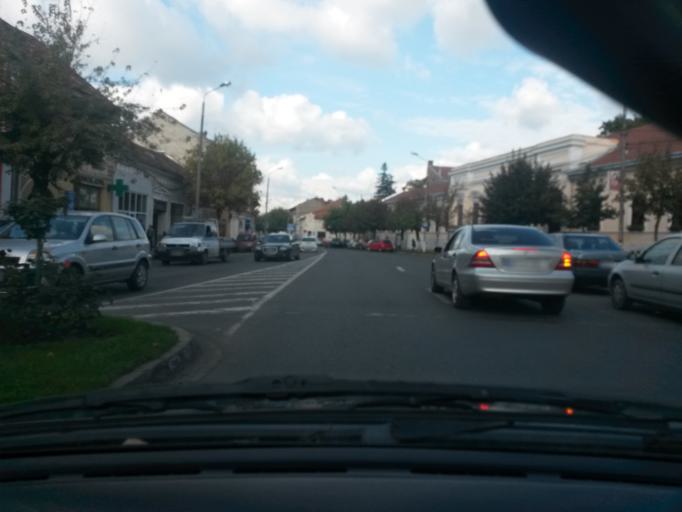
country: RO
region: Mures
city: Targu-Mures
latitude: 46.5474
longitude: 24.5641
